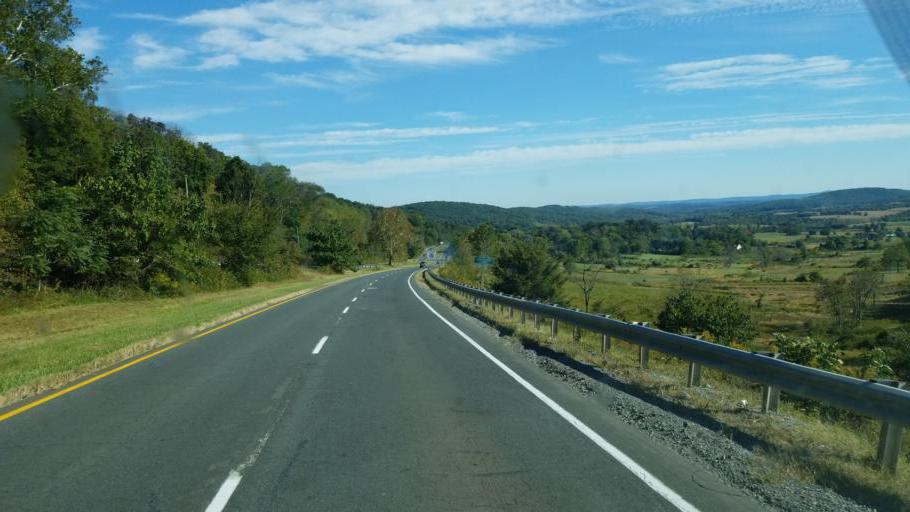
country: US
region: Virginia
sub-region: Warren County
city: Shenandoah Farms
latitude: 39.0125
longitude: -77.9604
